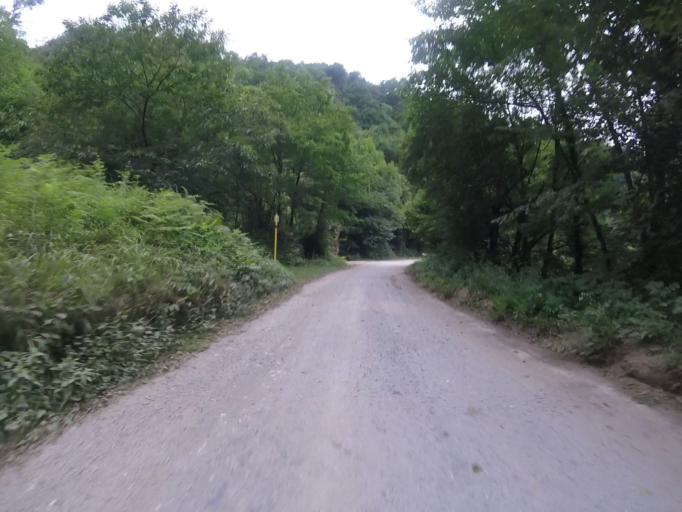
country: ES
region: Navarre
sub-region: Provincia de Navarra
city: Sunbilla
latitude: 43.1883
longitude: -1.6757
